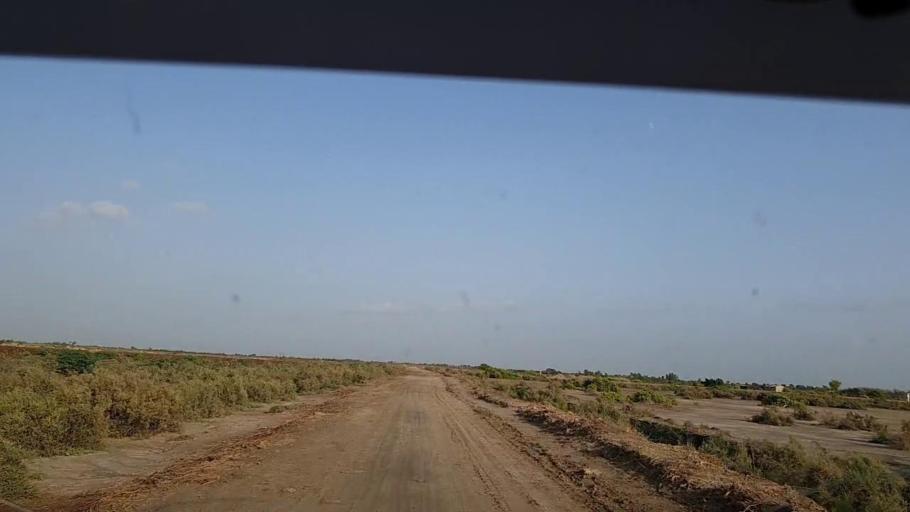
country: PK
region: Sindh
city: Badin
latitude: 24.5509
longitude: 68.8745
